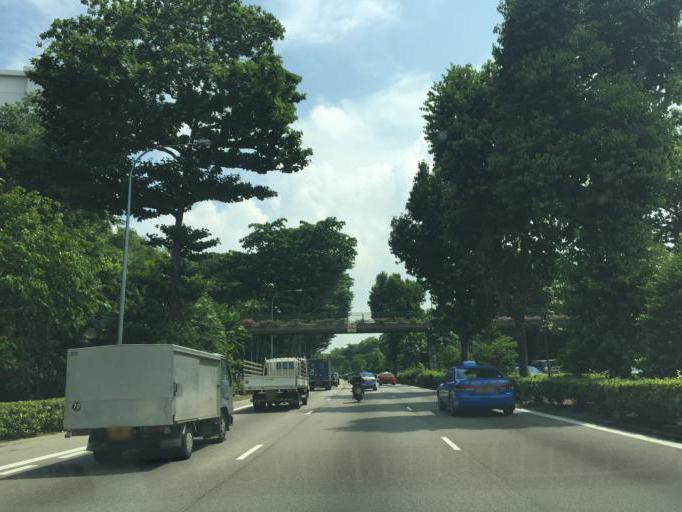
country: SG
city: Singapore
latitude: 1.3355
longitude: 103.9288
